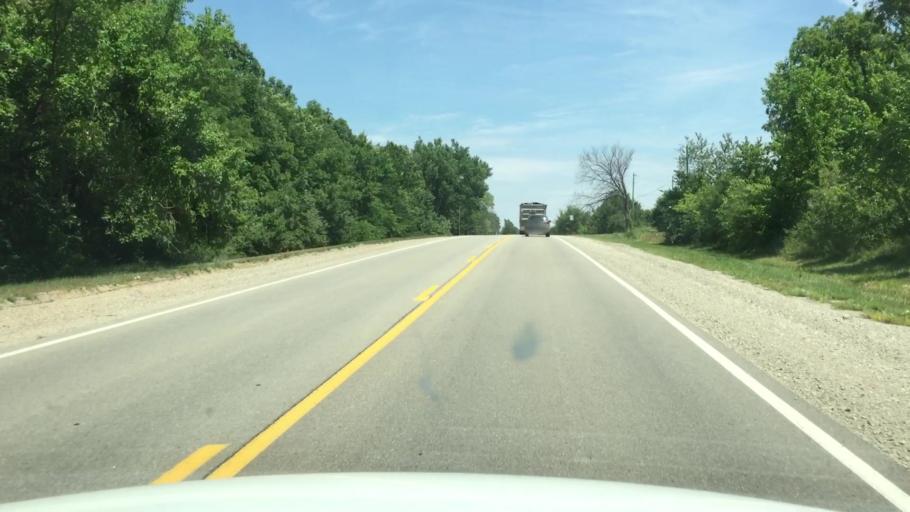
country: US
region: Kansas
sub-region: Shawnee County
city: Topeka
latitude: 38.9861
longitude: -95.5751
